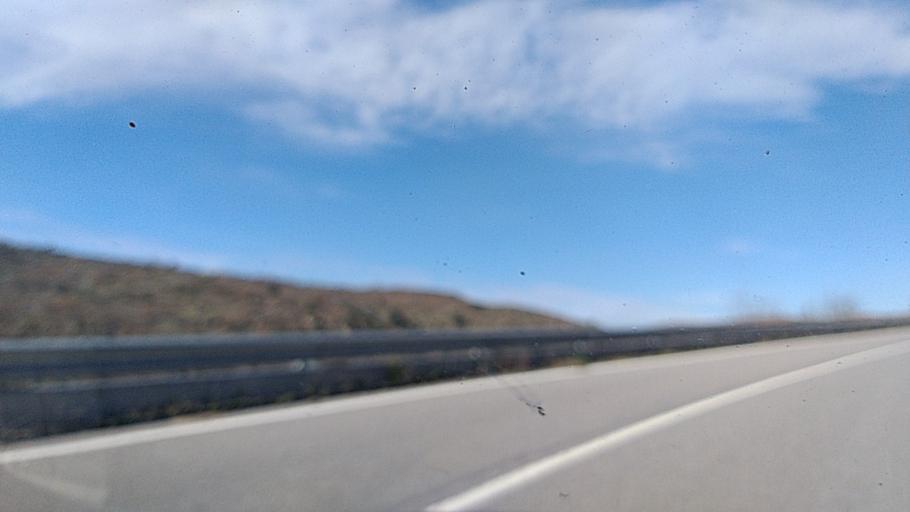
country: ES
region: Castille and Leon
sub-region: Provincia de Salamanca
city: Fuentes de Onoro
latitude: 40.6167
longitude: -6.9168
